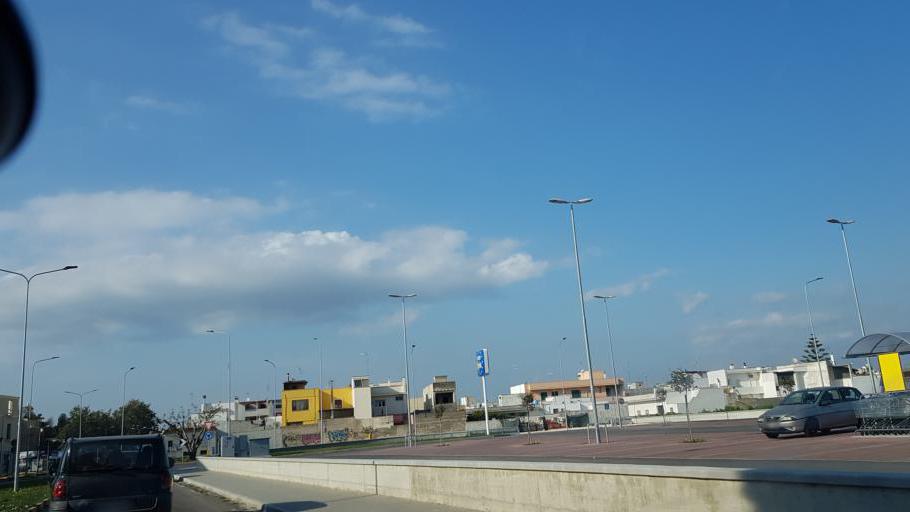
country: IT
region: Apulia
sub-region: Provincia di Brindisi
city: Mesagne
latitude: 40.5621
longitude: 17.8161
